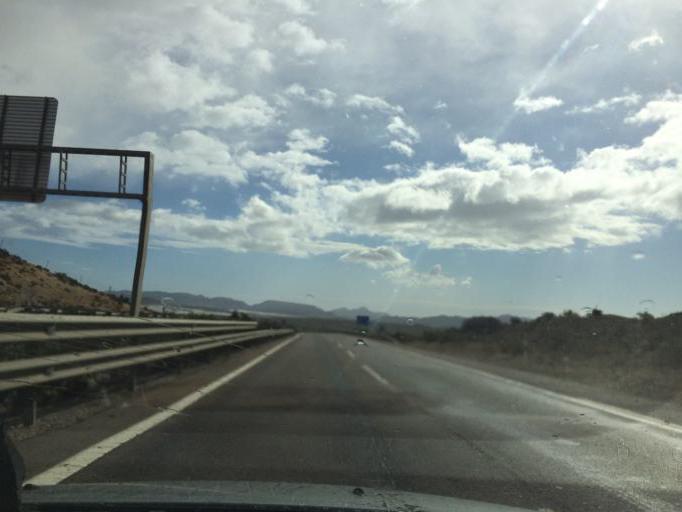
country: ES
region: Andalusia
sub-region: Provincia de Almeria
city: Retamar
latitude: 36.8629
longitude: -2.2632
